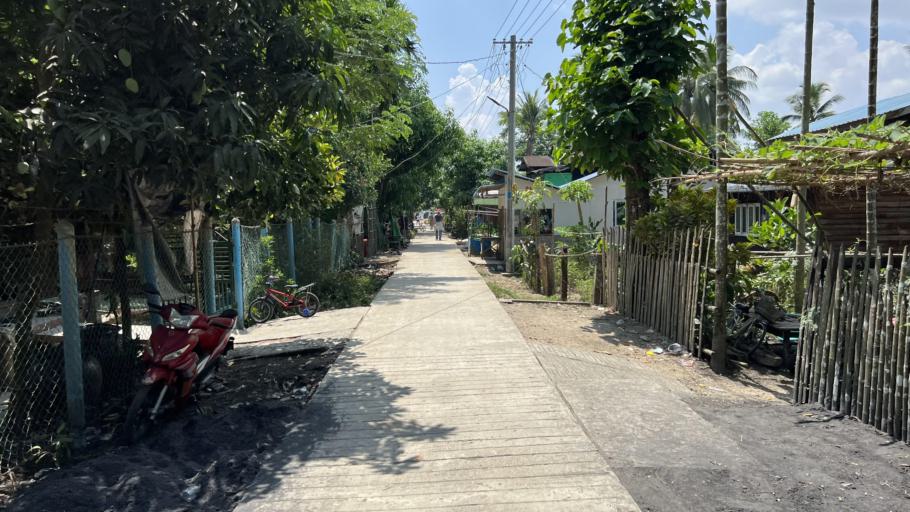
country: MM
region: Ayeyarwady
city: Kyaiklat
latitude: 16.4154
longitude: 95.8799
